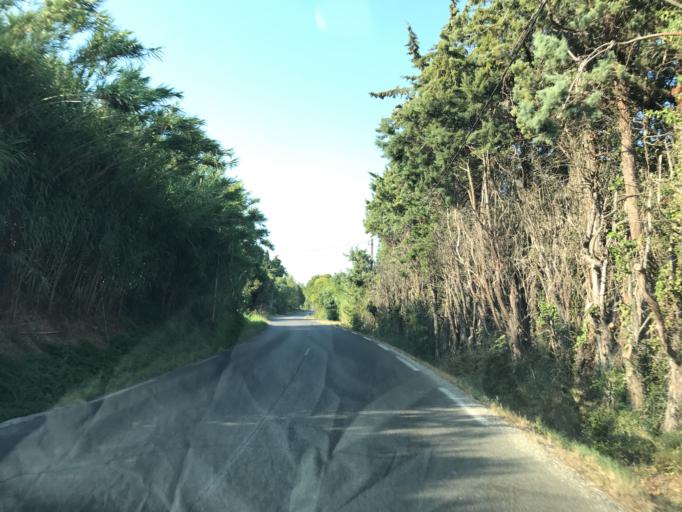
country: FR
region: Provence-Alpes-Cote d'Azur
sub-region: Departement des Bouches-du-Rhone
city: Saint-Chamas
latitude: 43.5616
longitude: 5.0157
